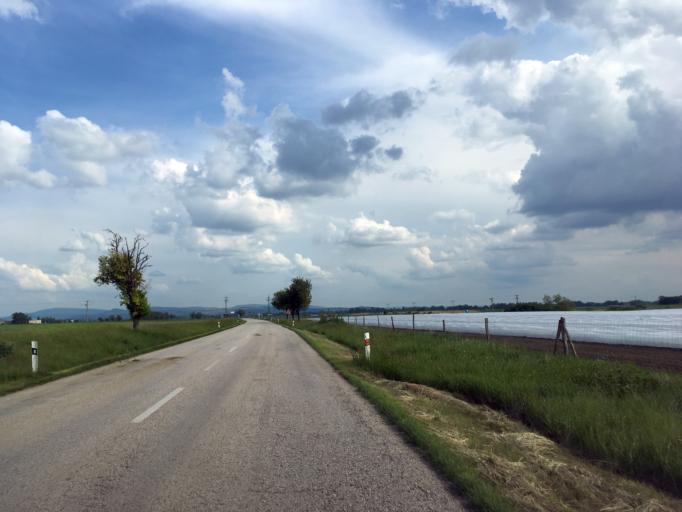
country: HU
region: Komarom-Esztergom
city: Almasfuzito
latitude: 47.7943
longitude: 18.2523
